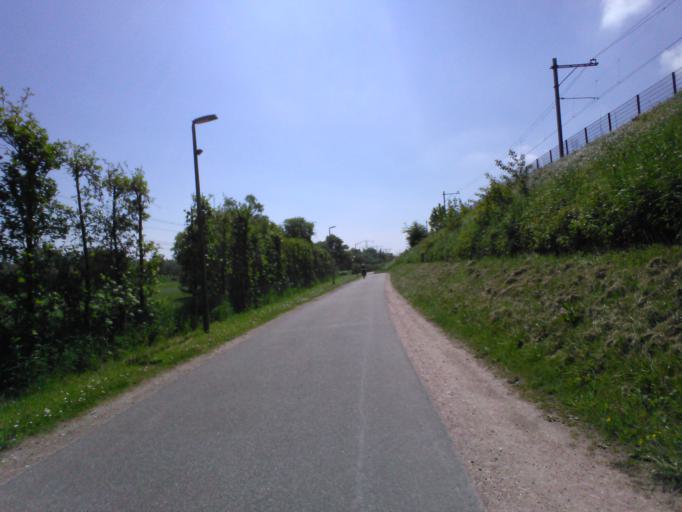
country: NL
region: South Holland
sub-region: Gemeente Sliedrecht
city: Sliedrecht
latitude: 51.8135
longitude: 4.7421
